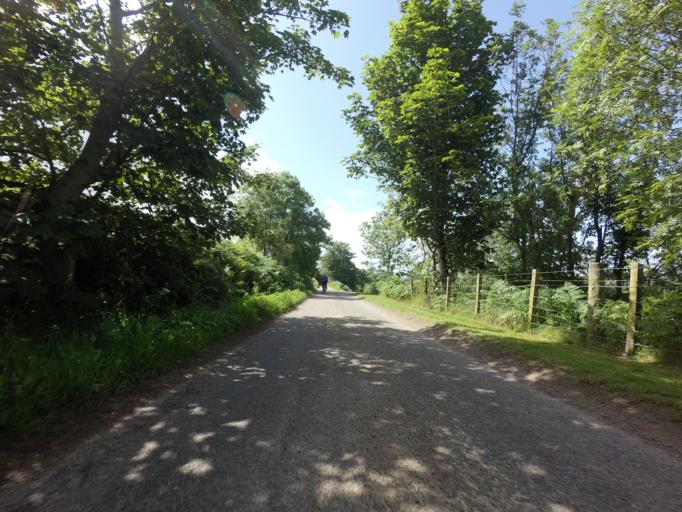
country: GB
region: Scotland
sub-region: Highland
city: Fortrose
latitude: 57.4897
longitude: -4.0184
